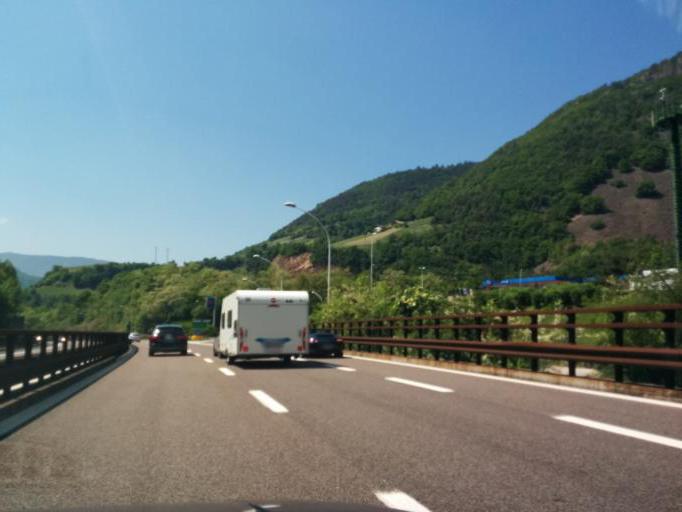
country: IT
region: Trentino-Alto Adige
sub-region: Bolzano
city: Fie Allo Sciliar
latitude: 46.5317
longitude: 11.4919
